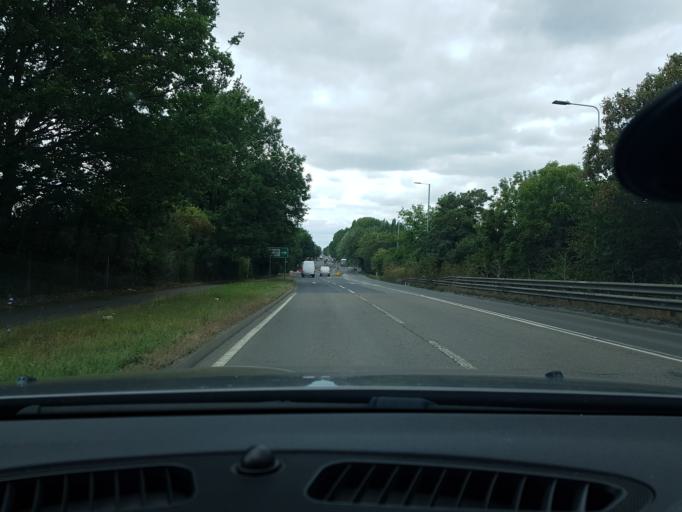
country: GB
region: England
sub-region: Surrey
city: Colnbrook
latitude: 51.4840
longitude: -0.5063
